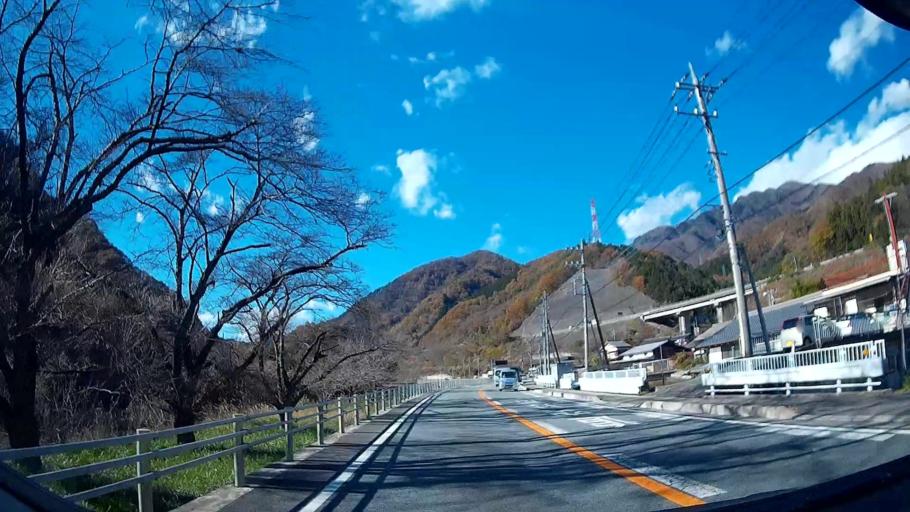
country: JP
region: Yamanashi
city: Otsuki
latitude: 35.6010
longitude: 138.8666
